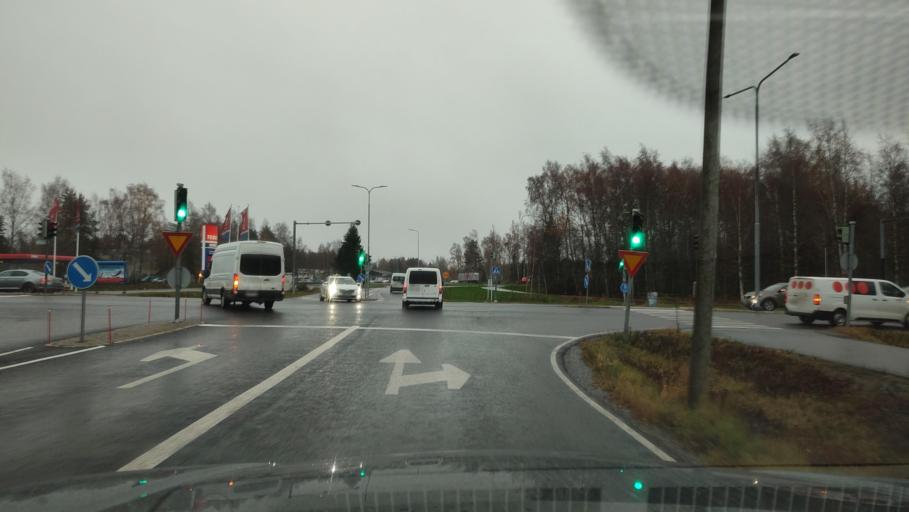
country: FI
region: Ostrobothnia
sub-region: Vaasa
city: Korsholm
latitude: 63.0900
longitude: 21.6548
